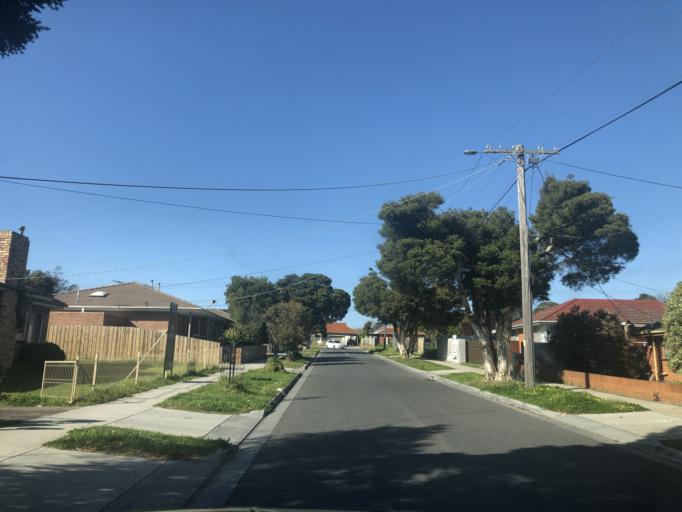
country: AU
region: Victoria
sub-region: Casey
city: Hampton Park
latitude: -38.0299
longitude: 145.2572
